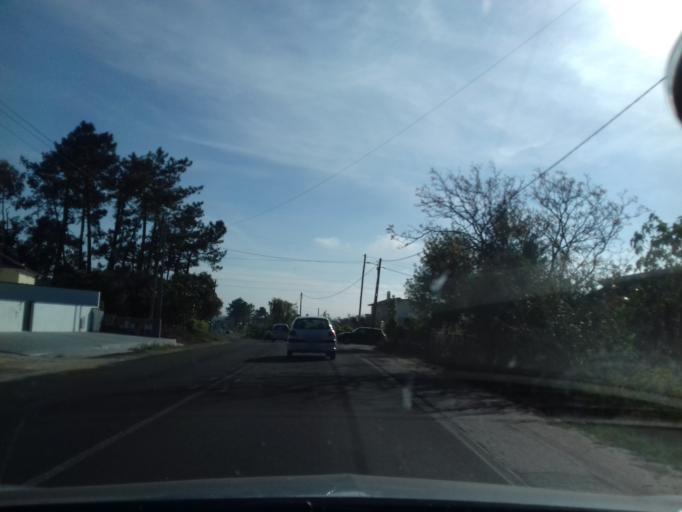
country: PT
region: Leiria
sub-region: Leiria
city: Maceira
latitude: 39.7004
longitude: -8.8745
